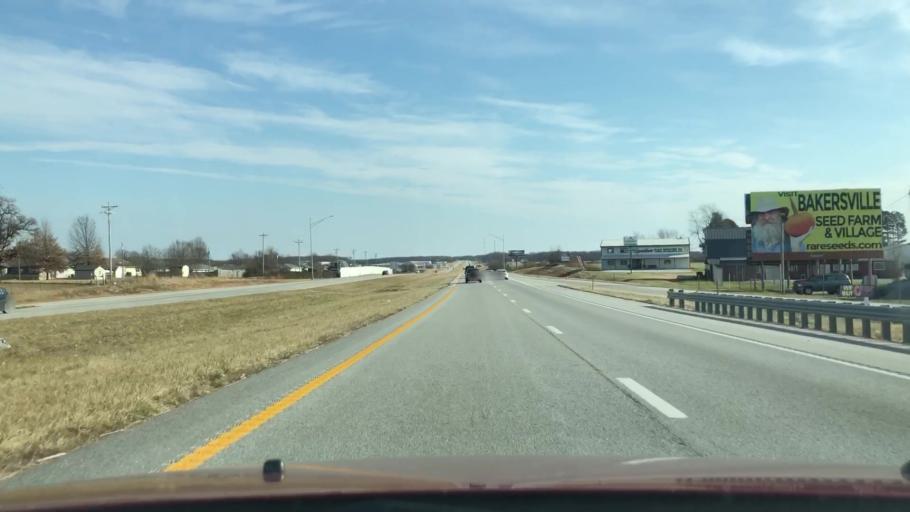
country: US
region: Missouri
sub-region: Webster County
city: Rogersville
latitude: 37.1112
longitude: -93.0534
